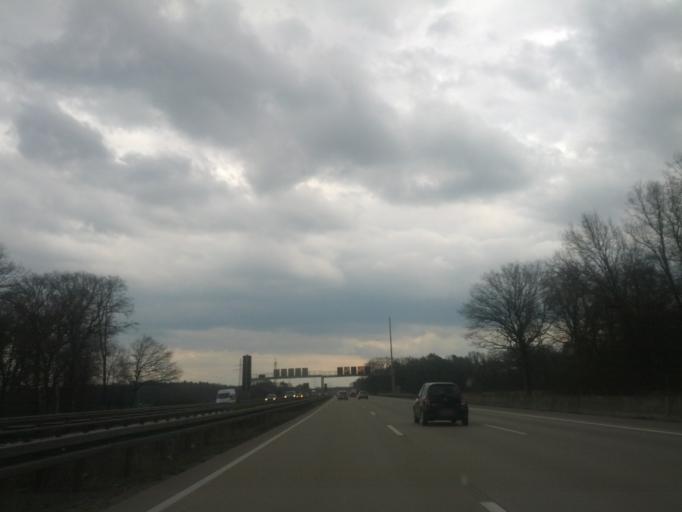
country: DE
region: Lower Saxony
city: Isernhagen Farster Bauerschaft
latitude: 52.5393
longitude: 9.8024
